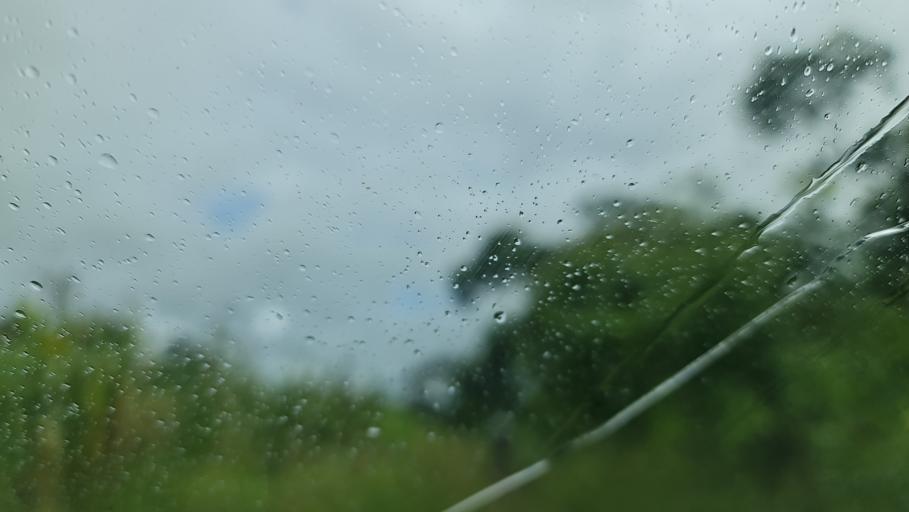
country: MW
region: Southern Region
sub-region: Nsanje District
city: Nsanje
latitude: -17.4465
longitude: 35.8432
